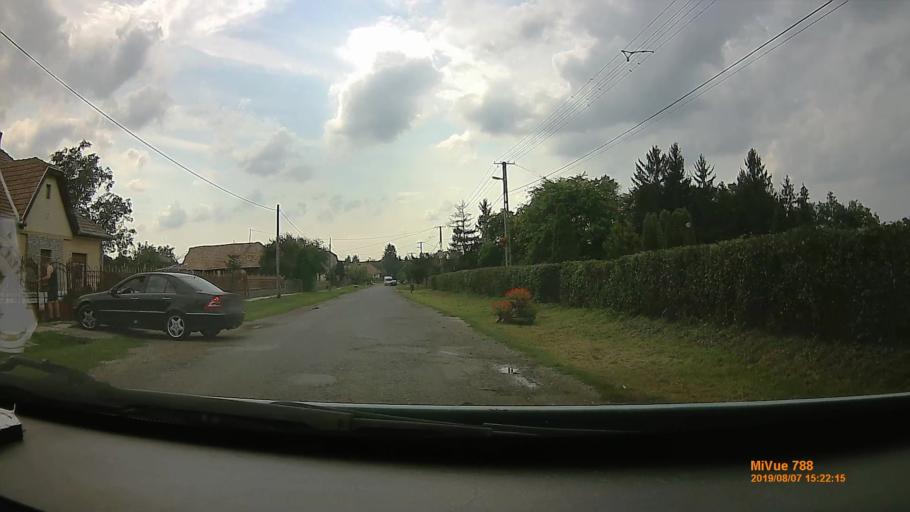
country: HU
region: Borsod-Abauj-Zemplen
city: Encs
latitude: 48.3615
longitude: 21.1447
